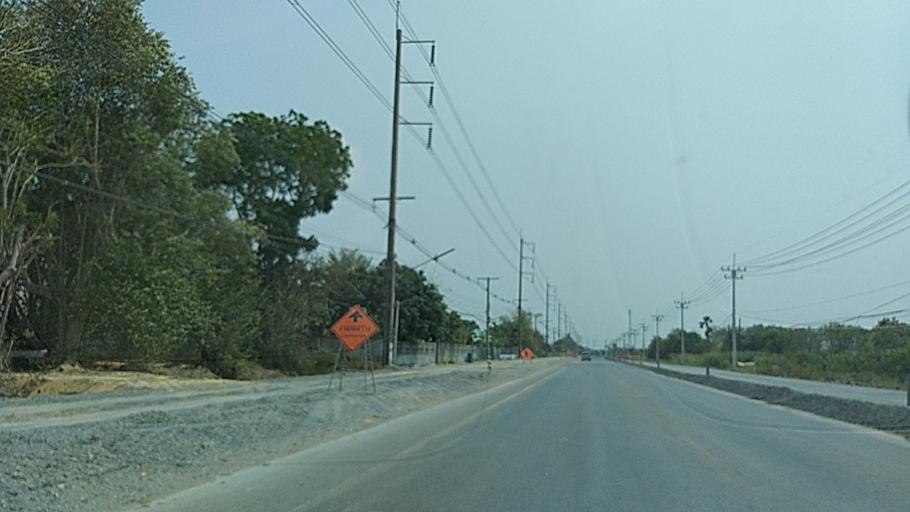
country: TH
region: Chachoengsao
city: Ban Pho
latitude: 13.5466
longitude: 101.1433
